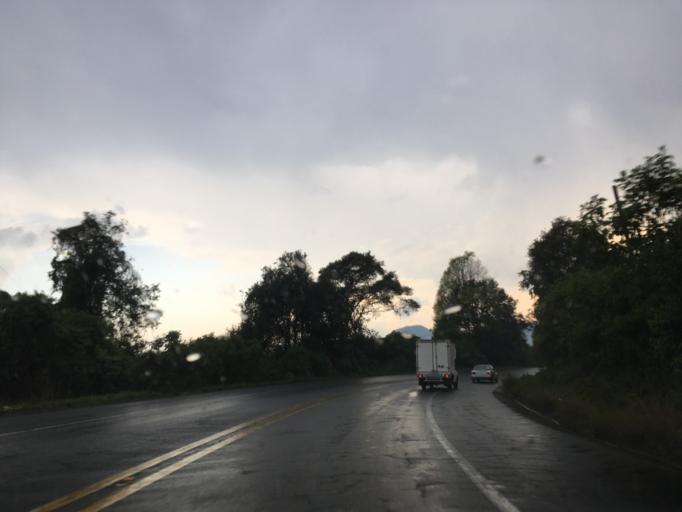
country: MX
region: Michoacan
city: Capacuaro
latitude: 19.5175
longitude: -102.0751
